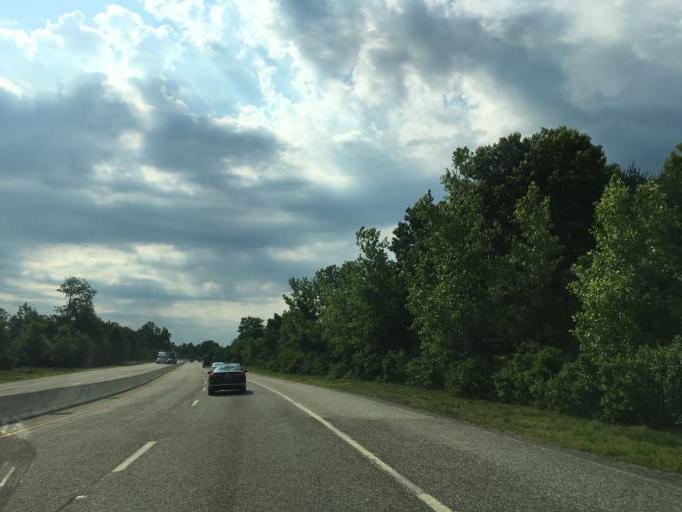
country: US
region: Rhode Island
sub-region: Kent County
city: East Greenwich
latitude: 41.6082
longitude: -71.4713
